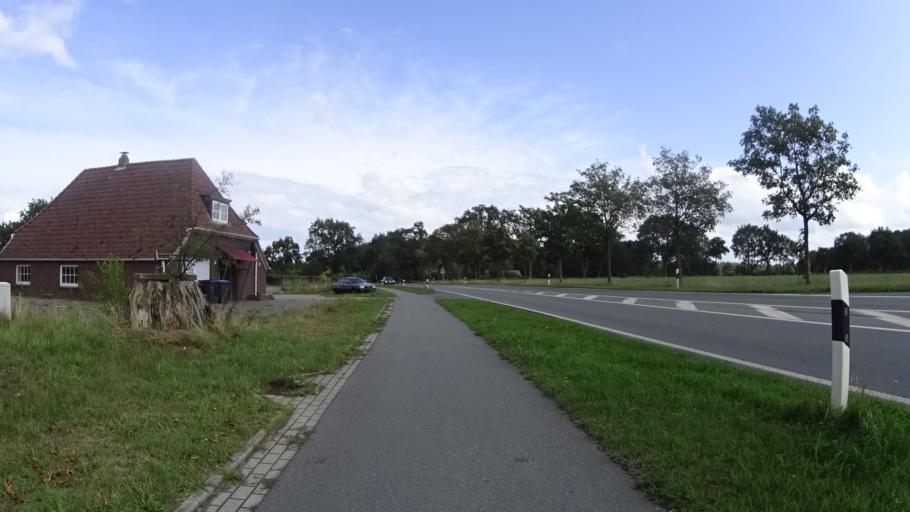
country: DE
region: Lower Saxony
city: Bockhorn
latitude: 53.3861
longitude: 8.0502
